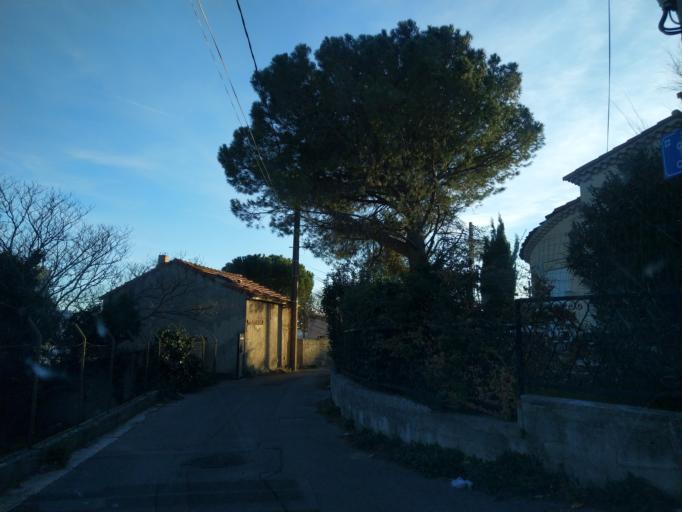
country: FR
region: Provence-Alpes-Cote d'Azur
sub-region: Departement des Bouches-du-Rhone
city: Plan-de-Cuques
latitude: 43.3566
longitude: 5.4619
